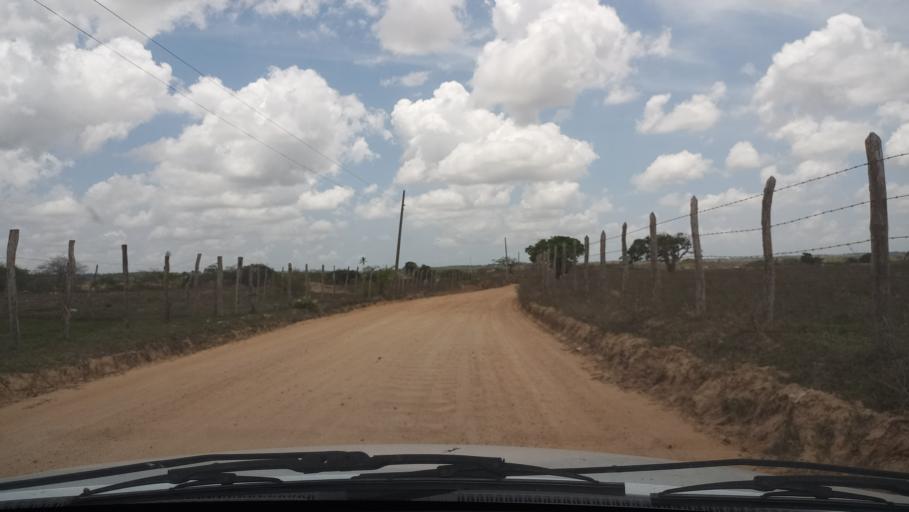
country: BR
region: Rio Grande do Norte
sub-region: Brejinho
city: Brejinho
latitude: -6.2829
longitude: -35.3415
